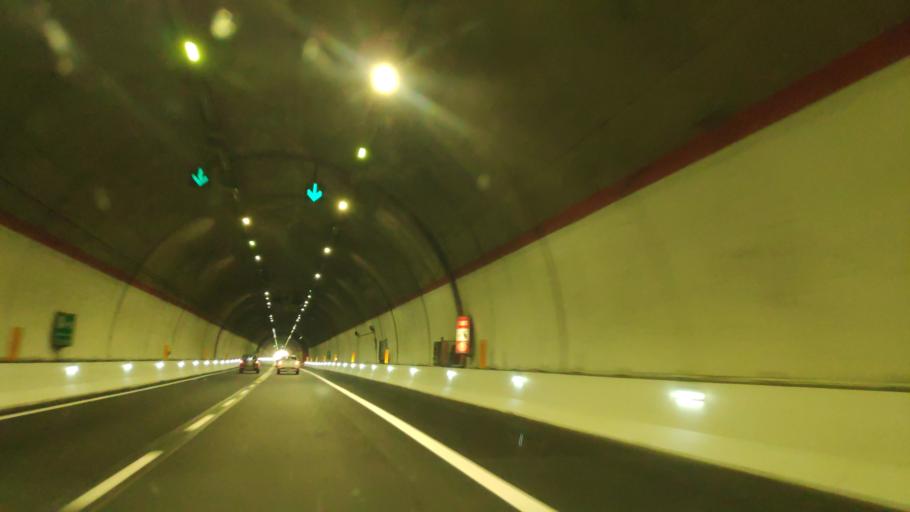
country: IT
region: Calabria
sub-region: Provincia di Reggio Calabria
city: Scilla
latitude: 38.2487
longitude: 15.7335
